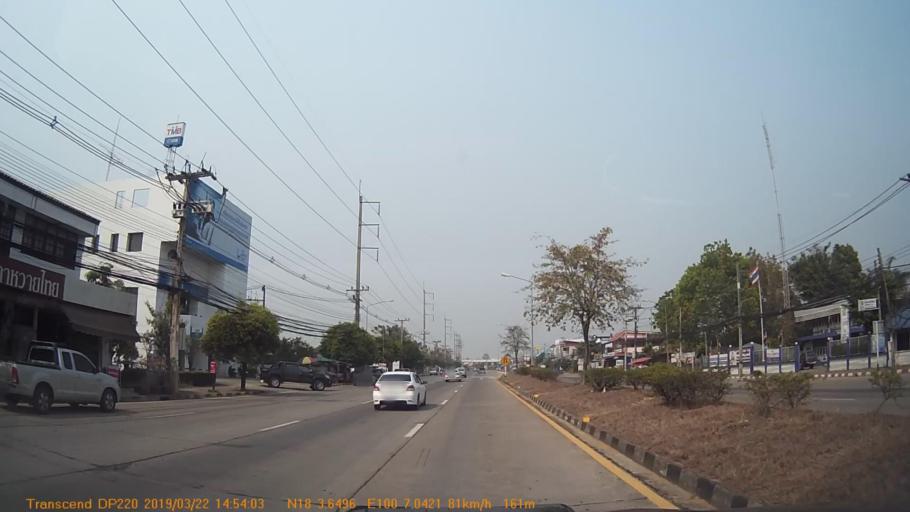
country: TH
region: Phrae
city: Sung Men
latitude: 18.0612
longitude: 100.1175
